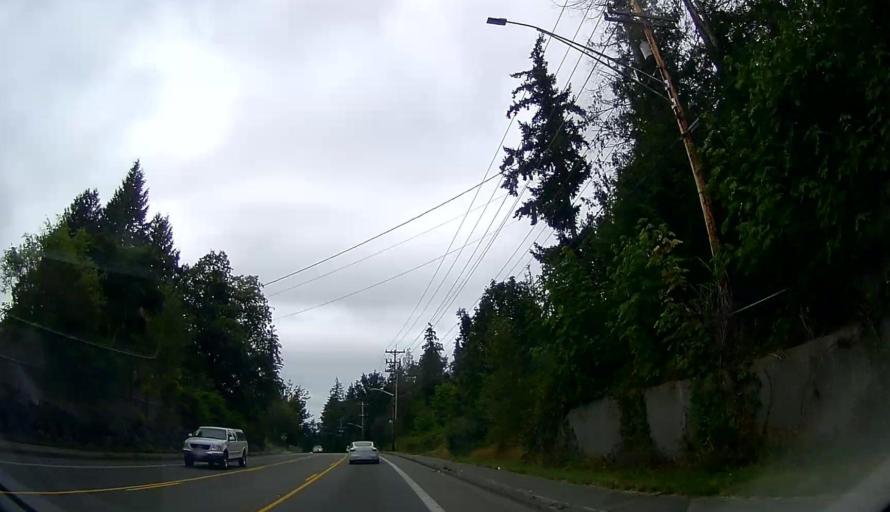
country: US
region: Washington
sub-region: Snohomish County
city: Marysville
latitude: 48.0493
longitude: -122.2141
